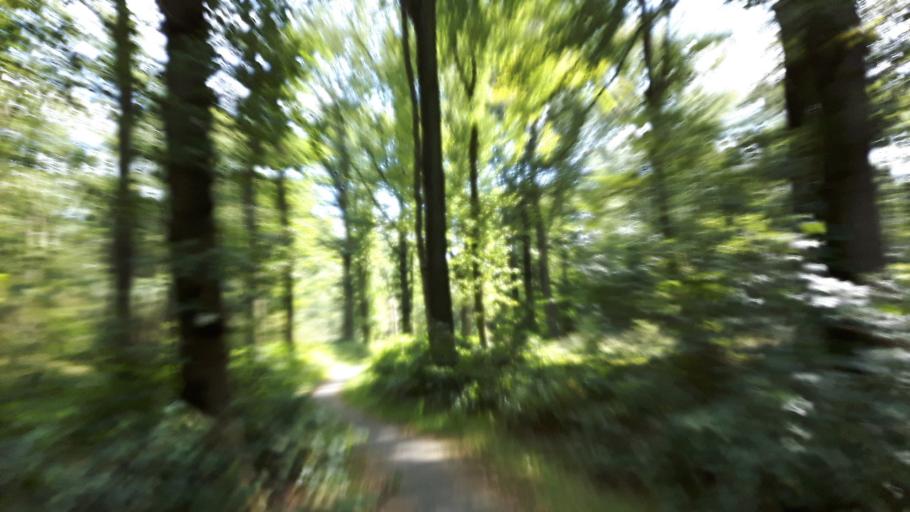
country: NL
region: Friesland
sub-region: Gemeente Smallingerland
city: Drachtstercompagnie
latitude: 53.0687
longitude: 6.2068
